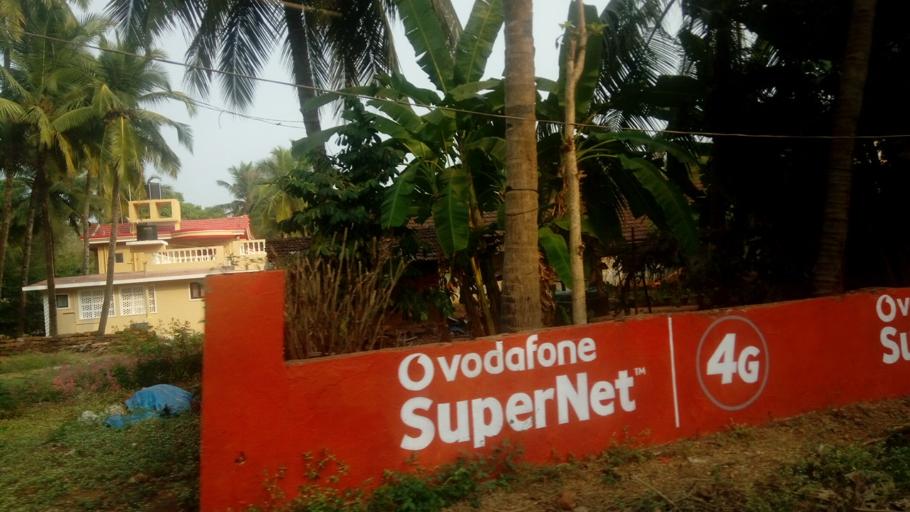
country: IN
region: Goa
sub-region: South Goa
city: Varca
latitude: 15.2369
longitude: 73.9427
